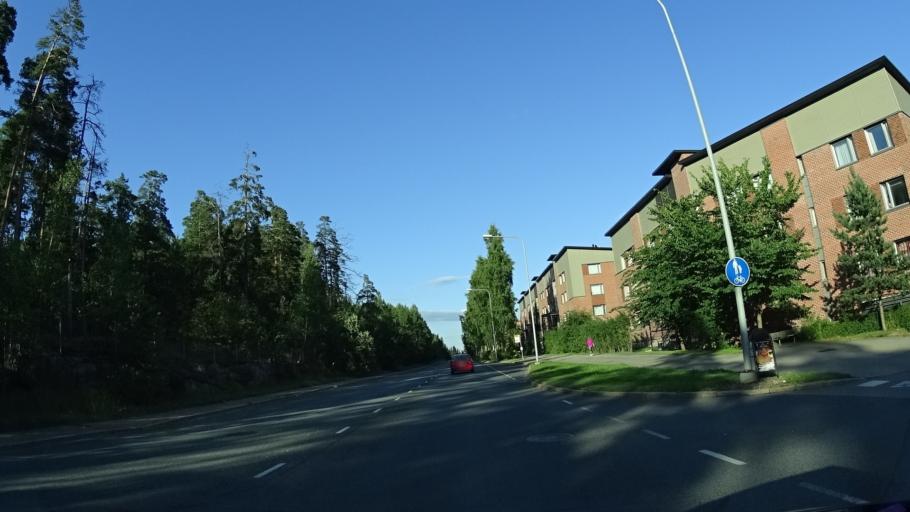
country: FI
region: Uusimaa
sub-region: Helsinki
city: Teekkarikylae
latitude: 60.2477
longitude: 24.8581
